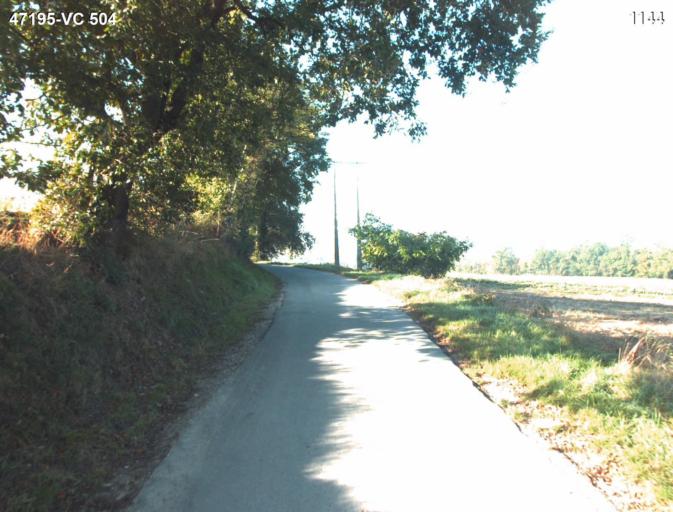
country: FR
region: Aquitaine
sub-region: Departement du Lot-et-Garonne
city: Nerac
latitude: 44.1570
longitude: 0.3342
